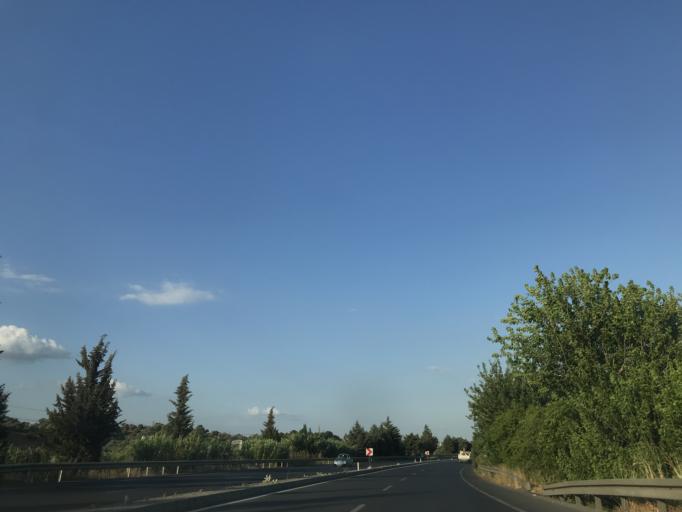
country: TR
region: Aydin
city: Kosk
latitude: 37.8554
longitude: 28.0839
